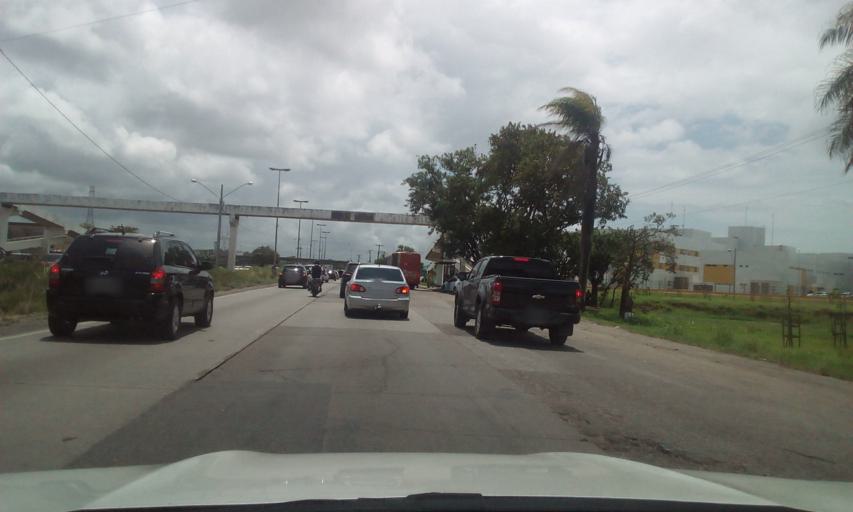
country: BR
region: Pernambuco
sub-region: Recife
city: Recife
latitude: -8.0722
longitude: -34.9425
